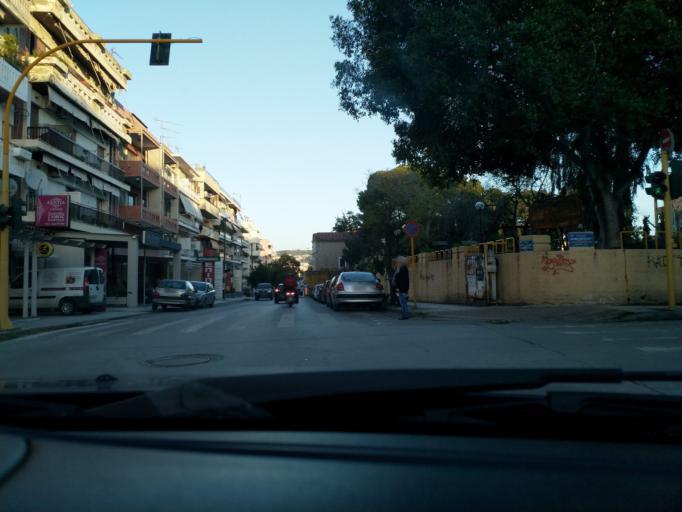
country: GR
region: Crete
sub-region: Nomos Chanias
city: Chania
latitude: 35.5101
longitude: 24.0139
